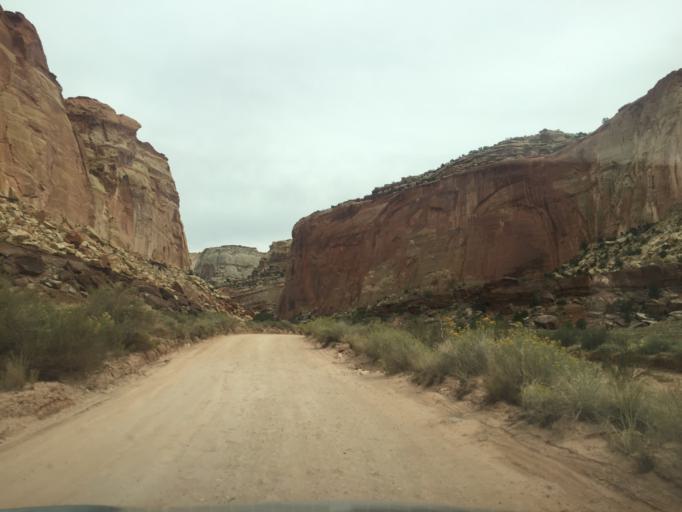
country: US
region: Utah
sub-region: Wayne County
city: Loa
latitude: 38.2587
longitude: -111.2282
